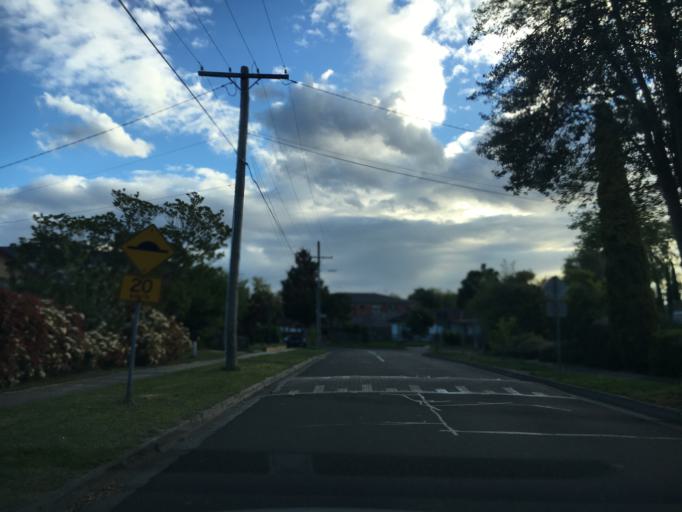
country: AU
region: Victoria
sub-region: Whitehorse
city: Vermont South
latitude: -37.8841
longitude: 145.1672
